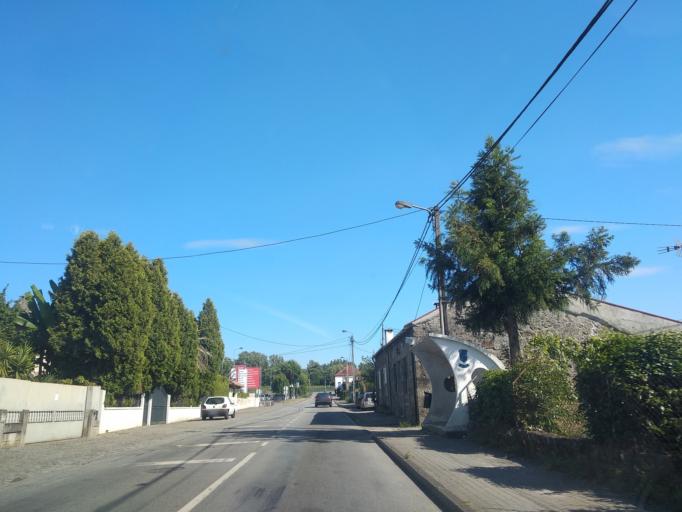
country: PT
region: Braga
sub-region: Vila Verde
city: Prado
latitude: 41.5929
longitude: -8.4606
